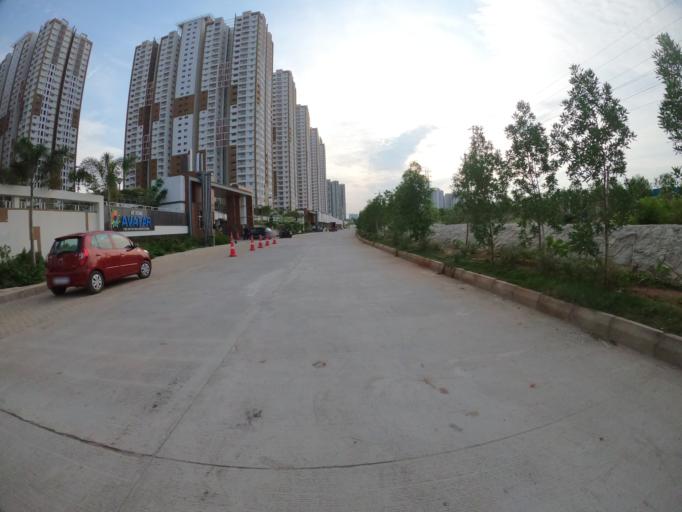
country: IN
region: Telangana
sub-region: Hyderabad
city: Hyderabad
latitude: 17.3995
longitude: 78.3569
